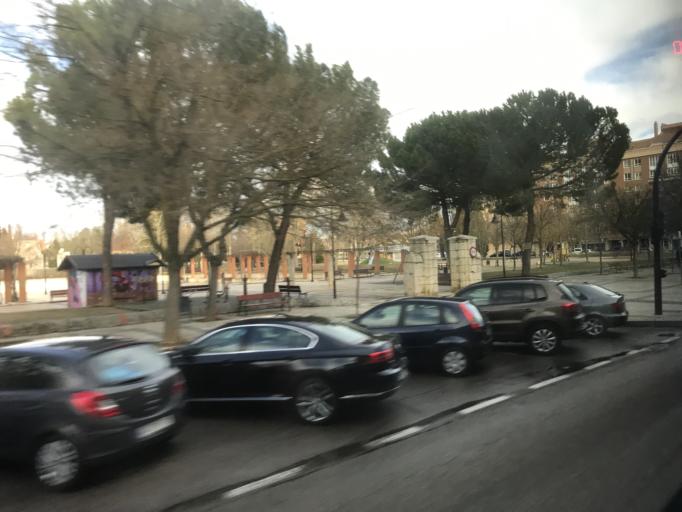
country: ES
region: Castille and Leon
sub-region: Provincia de Palencia
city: Palencia
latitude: 42.0185
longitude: -4.5415
